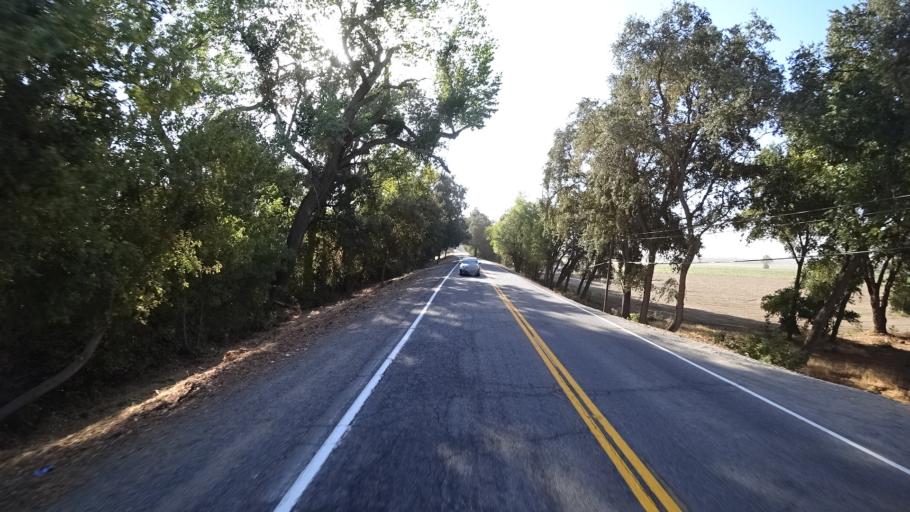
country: US
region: California
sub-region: Yolo County
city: West Sacramento
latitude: 38.4885
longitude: -121.5547
